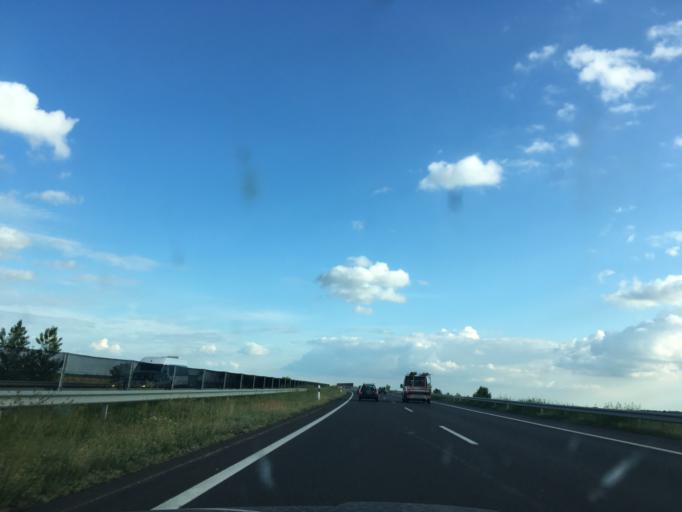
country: HU
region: Hajdu-Bihar
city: Polgar
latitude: 47.8281
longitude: 21.1506
